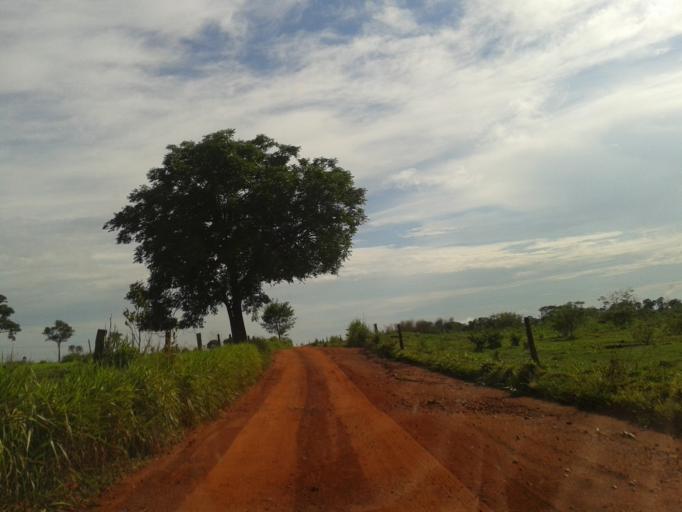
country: BR
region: Minas Gerais
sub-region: Santa Vitoria
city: Santa Vitoria
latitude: -19.2133
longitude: -50.6702
